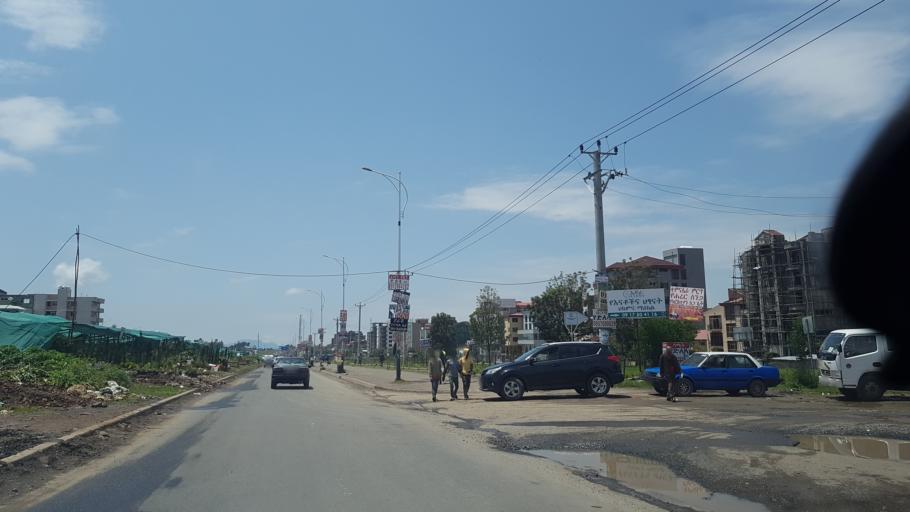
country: ET
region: Adis Abeba
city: Addis Ababa
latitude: 9.0140
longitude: 38.8520
